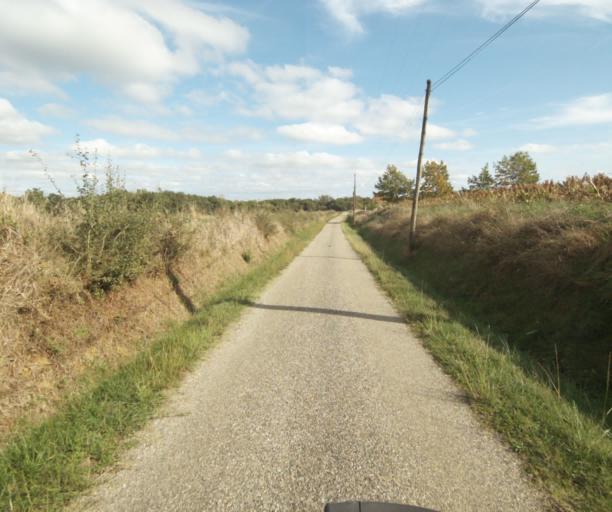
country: FR
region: Midi-Pyrenees
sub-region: Departement du Tarn-et-Garonne
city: Saint-Porquier
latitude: 43.9371
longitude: 1.1244
